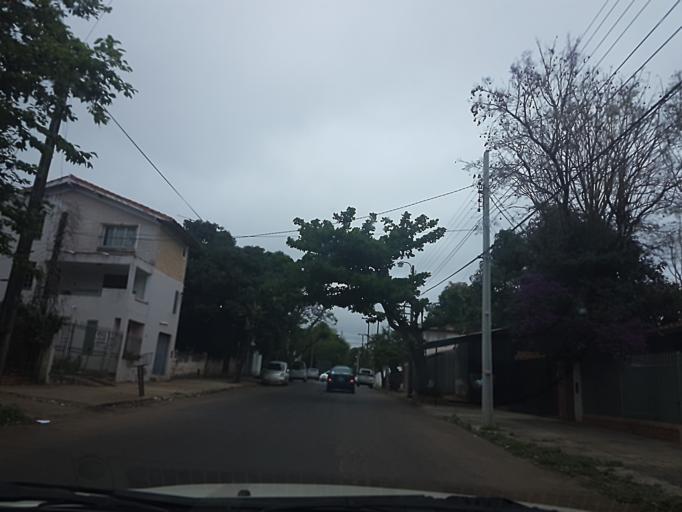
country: PY
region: Central
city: Lambare
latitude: -25.3340
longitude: -57.5685
